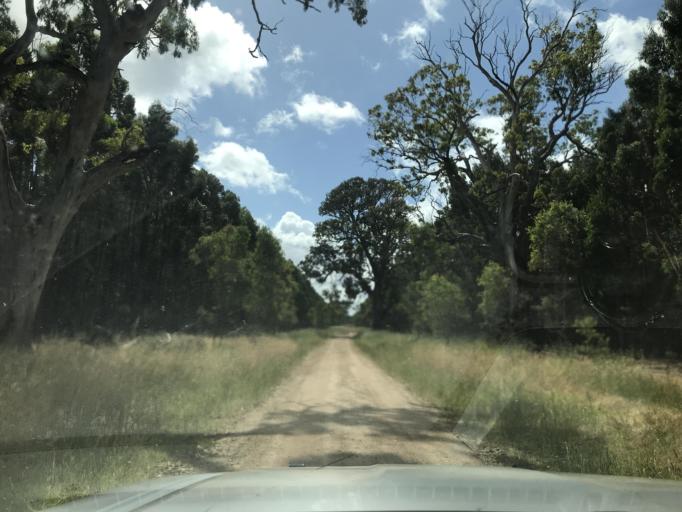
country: AU
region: South Australia
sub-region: Wattle Range
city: Penola
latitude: -37.1904
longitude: 141.3829
